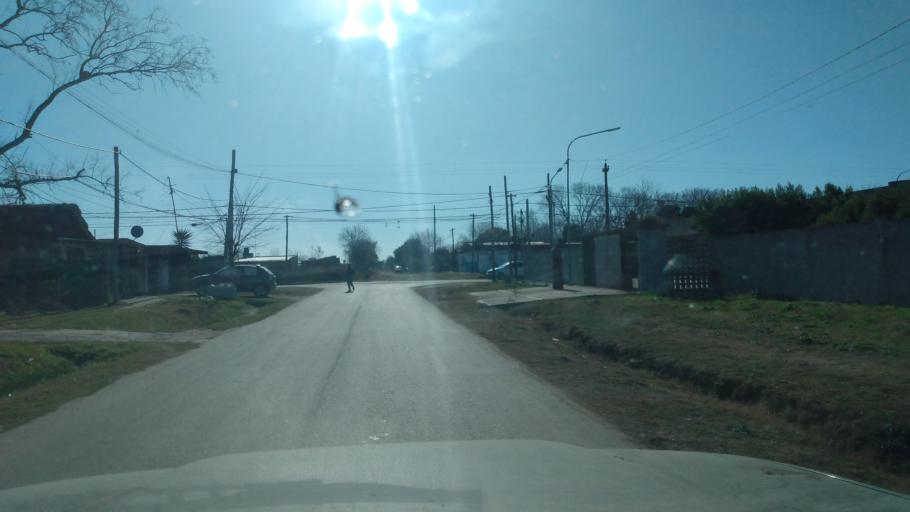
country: AR
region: Buenos Aires
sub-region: Partido de Lujan
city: Lujan
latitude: -34.5672
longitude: -59.0830
